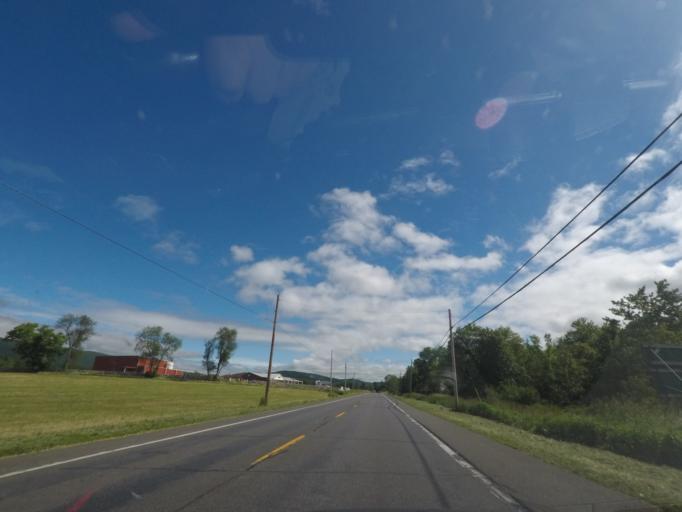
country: US
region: New York
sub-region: Dutchess County
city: Pine Plains
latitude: 42.0887
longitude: -73.5439
